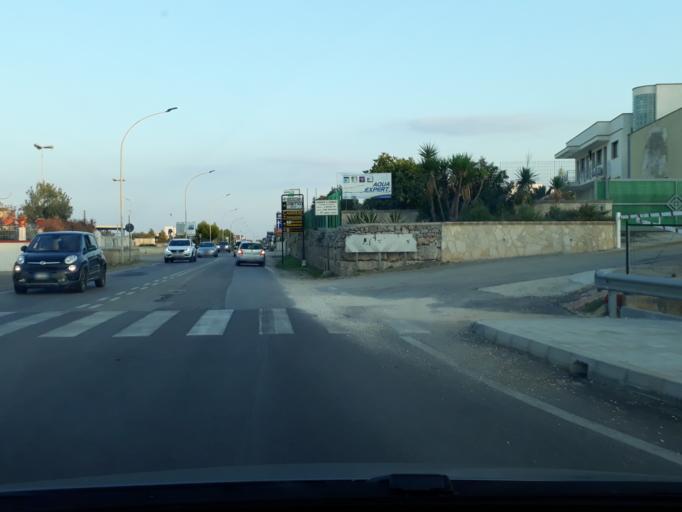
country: IT
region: Apulia
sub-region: Provincia di Bari
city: Monopoli
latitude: 40.9707
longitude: 17.2647
